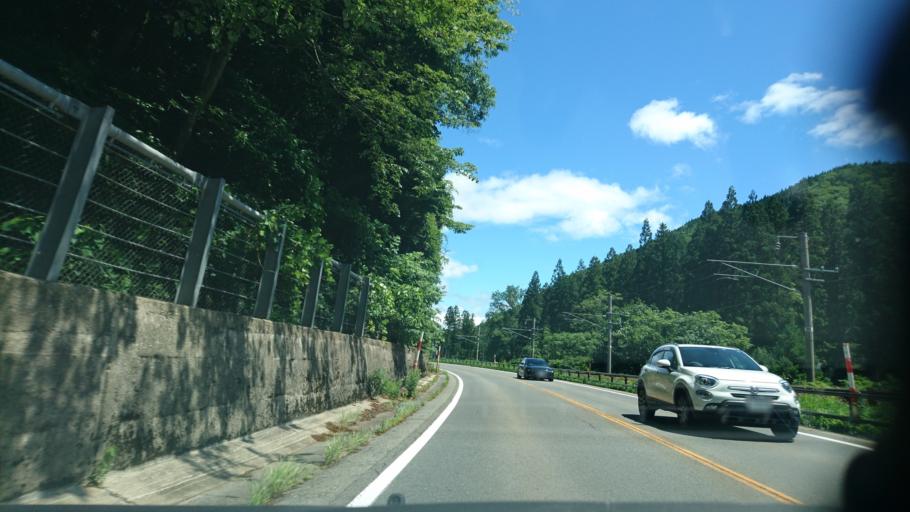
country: JP
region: Akita
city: Kakunodatemachi
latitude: 39.6449
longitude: 140.6638
